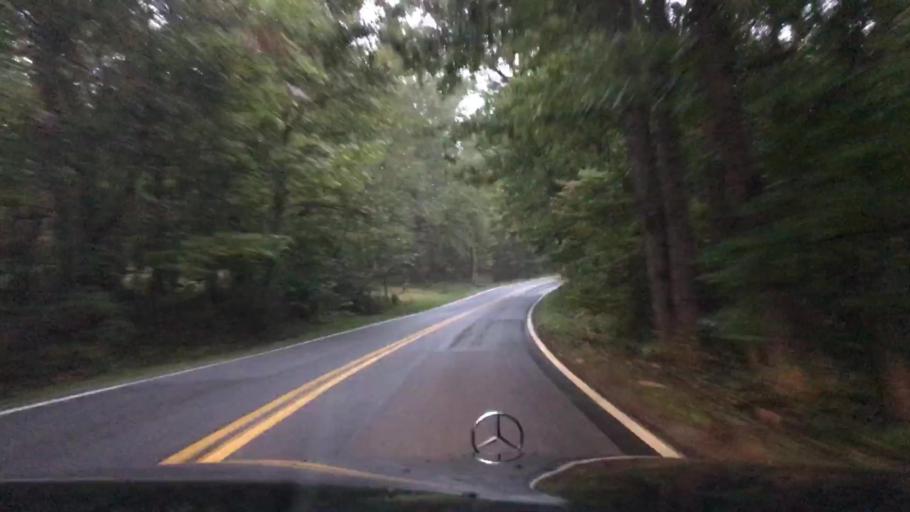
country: US
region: Virginia
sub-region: Campbell County
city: Timberlake
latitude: 37.2456
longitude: -79.2822
